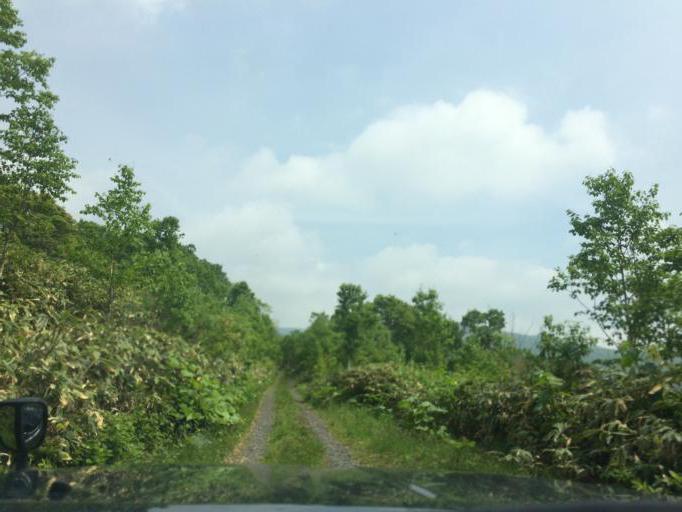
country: JP
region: Hokkaido
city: Niseko Town
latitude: 42.6803
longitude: 140.6131
